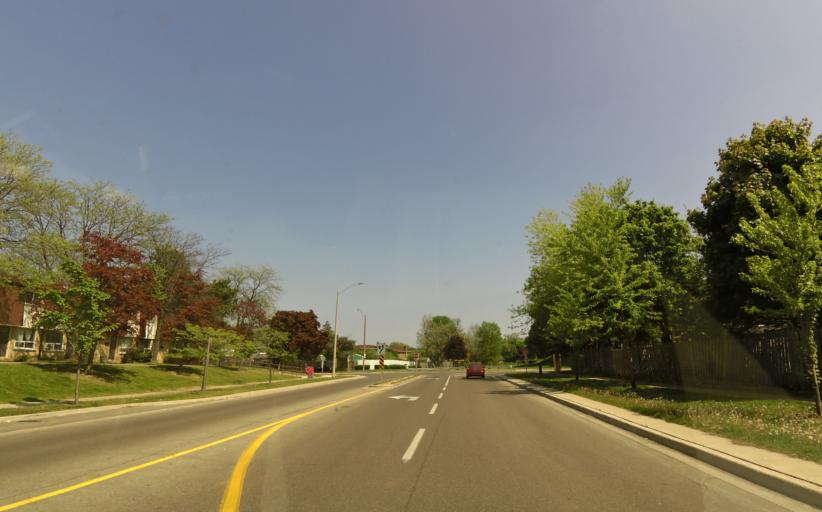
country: CA
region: Ontario
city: Mississauga
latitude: 43.5913
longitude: -79.6146
